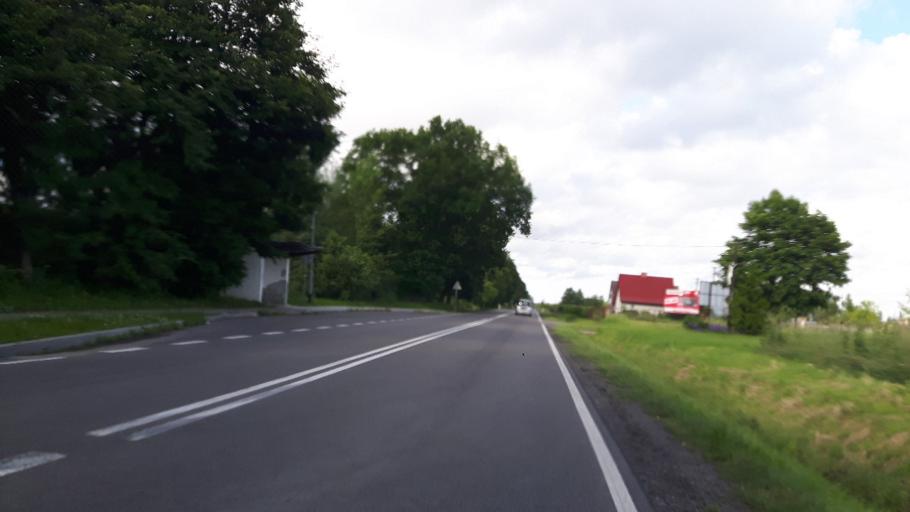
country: PL
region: West Pomeranian Voivodeship
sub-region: Powiat kolobrzeski
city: Ustronie Morskie
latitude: 54.1919
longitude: 15.6958
